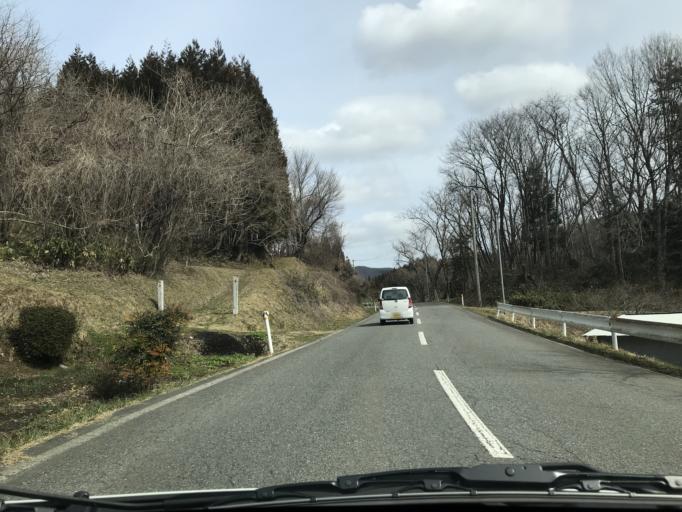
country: JP
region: Iwate
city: Kitakami
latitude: 39.2400
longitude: 141.3159
